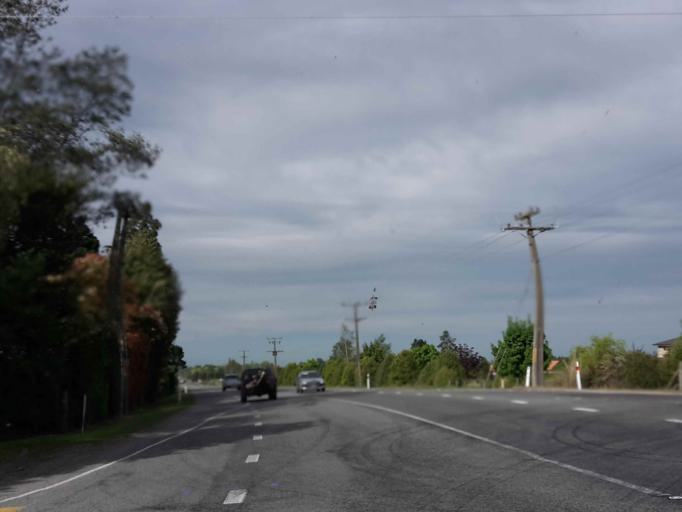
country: NZ
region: Canterbury
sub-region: Timaru District
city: Pleasant Point
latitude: -44.1124
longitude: 171.2239
